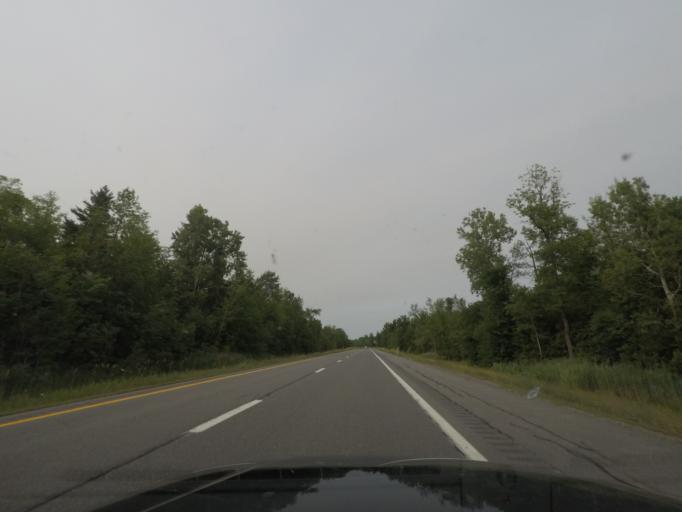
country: US
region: New York
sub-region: Clinton County
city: Champlain
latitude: 44.9113
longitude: -73.4494
